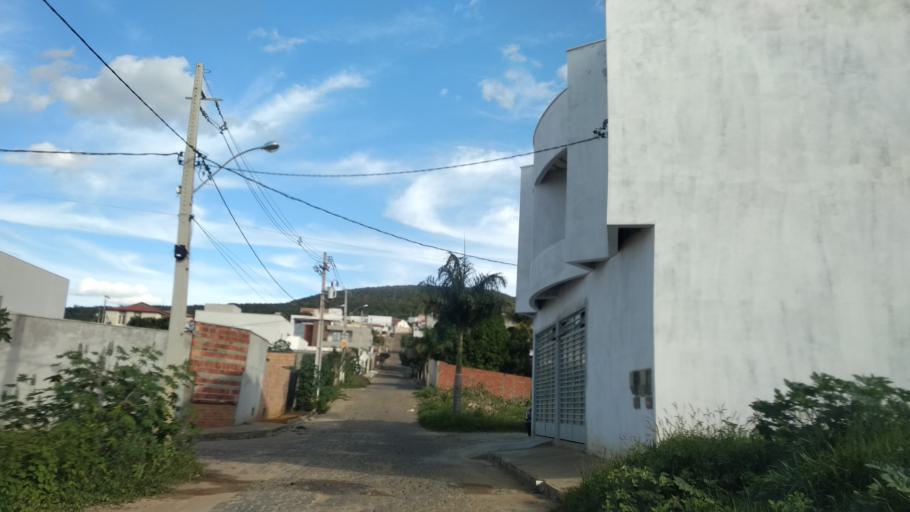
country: BR
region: Bahia
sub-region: Caetite
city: Caetite
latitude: -14.0730
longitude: -42.4836
